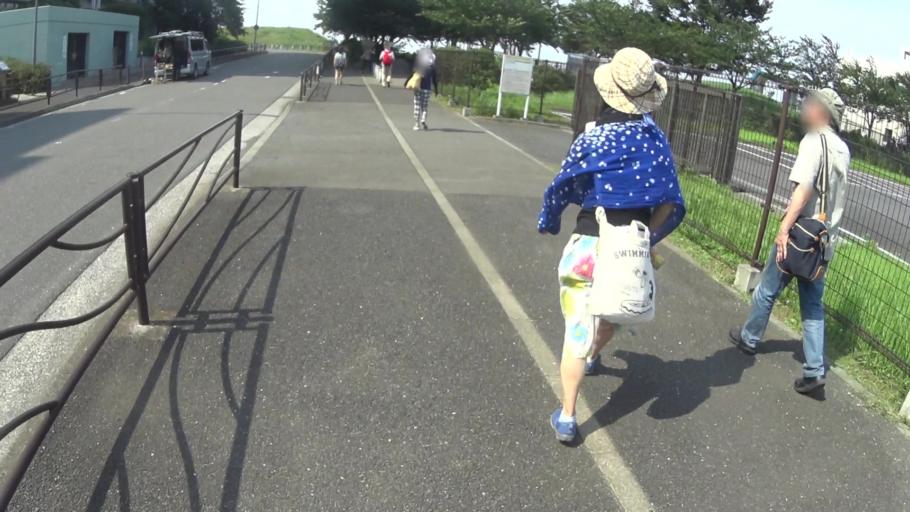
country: JP
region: Kanagawa
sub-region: Kawasaki-shi
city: Kawasaki
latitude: 35.5399
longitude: 139.7362
